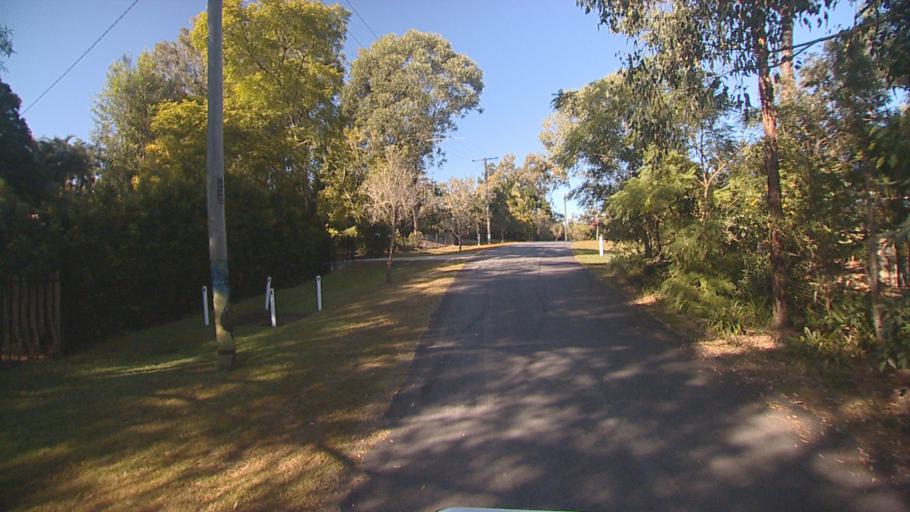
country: AU
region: Queensland
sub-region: Brisbane
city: Forest Lake
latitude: -27.6675
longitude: 153.0034
